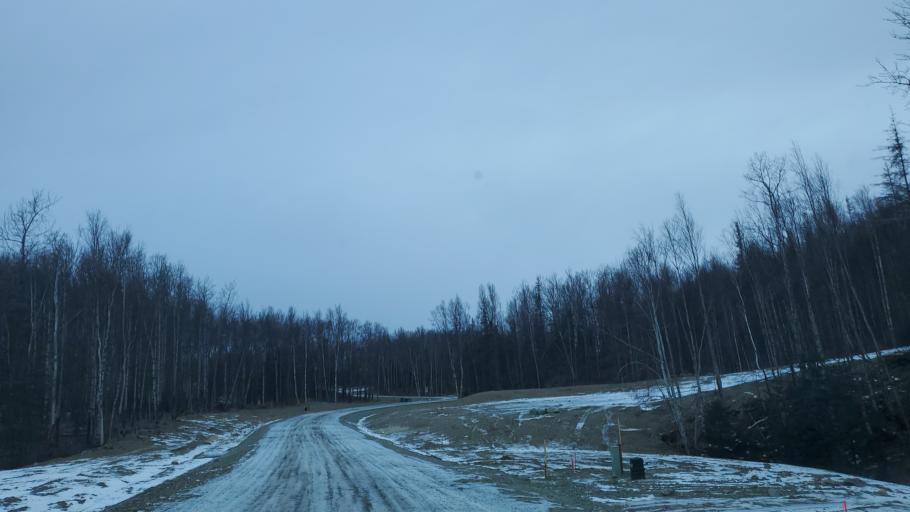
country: US
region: Alaska
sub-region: Matanuska-Susitna Borough
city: Gateway
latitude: 61.6554
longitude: -149.2324
